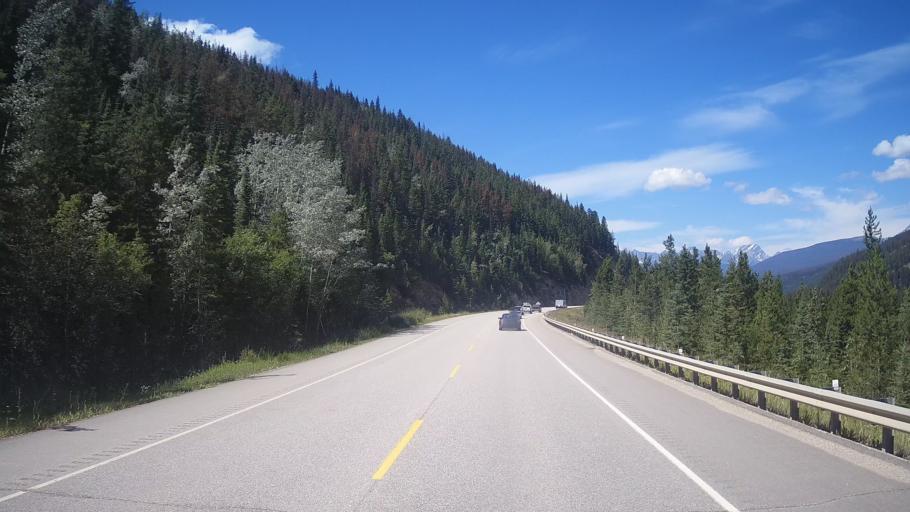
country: CA
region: Alberta
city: Jasper Park Lodge
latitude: 52.8728
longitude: -118.2982
